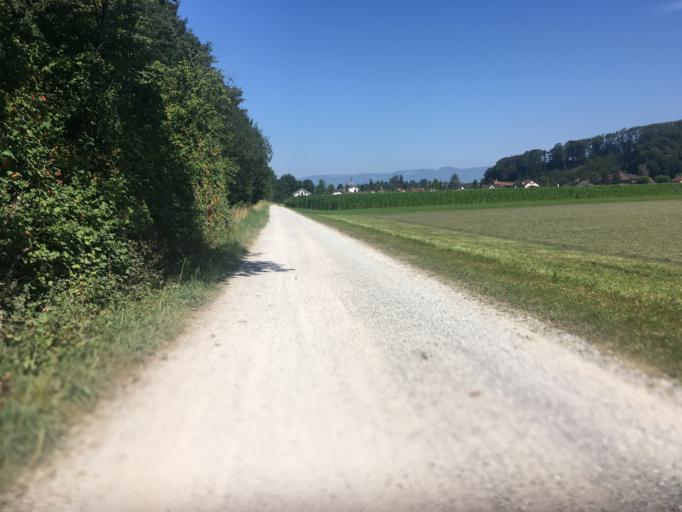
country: CH
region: Bern
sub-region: Emmental District
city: Lyssach
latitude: 47.0723
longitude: 7.5996
